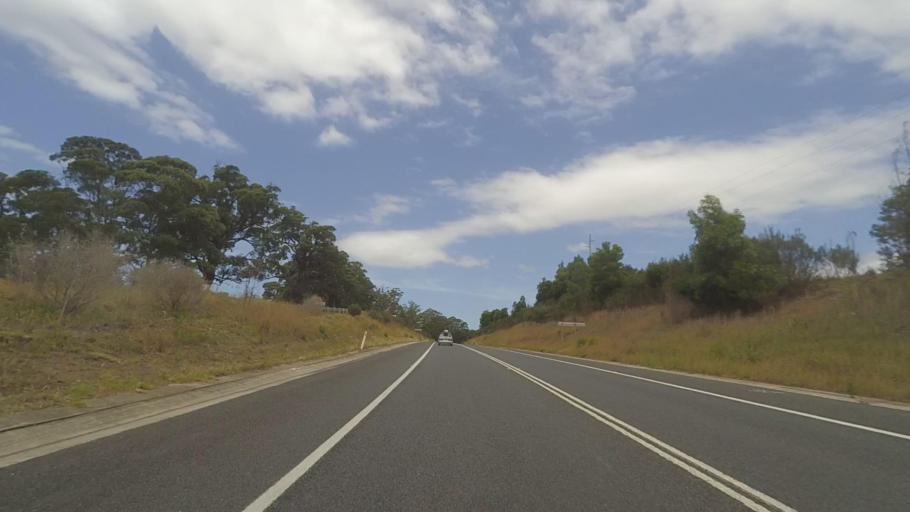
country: AU
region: New South Wales
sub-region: Shoalhaven Shire
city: Milton
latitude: -35.2201
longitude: 150.4351
